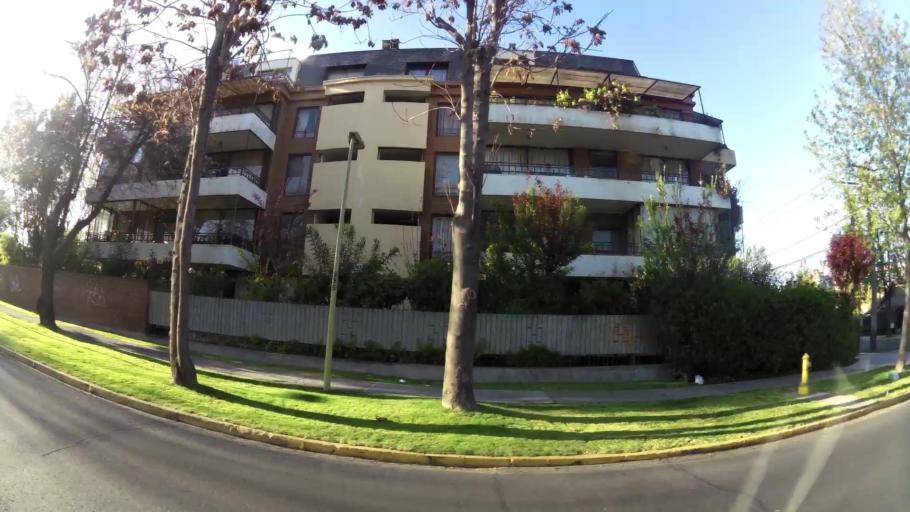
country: CL
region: Santiago Metropolitan
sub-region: Provincia de Santiago
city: Villa Presidente Frei, Nunoa, Santiago, Chile
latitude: -33.3971
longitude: -70.5603
